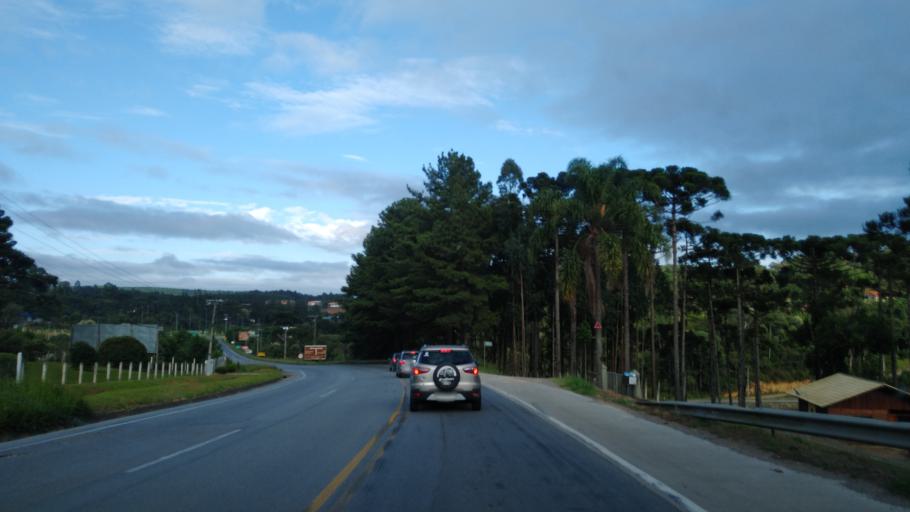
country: BR
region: Santa Catarina
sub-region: Rio Negrinho
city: Rio Negrinho
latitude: -26.2442
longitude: -49.4567
